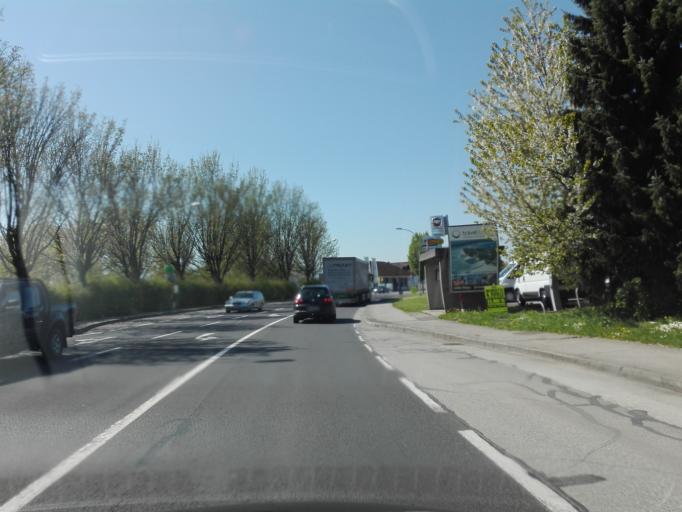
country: AT
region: Upper Austria
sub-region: Steyr Stadt
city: Steyr
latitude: 48.0473
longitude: 14.4138
